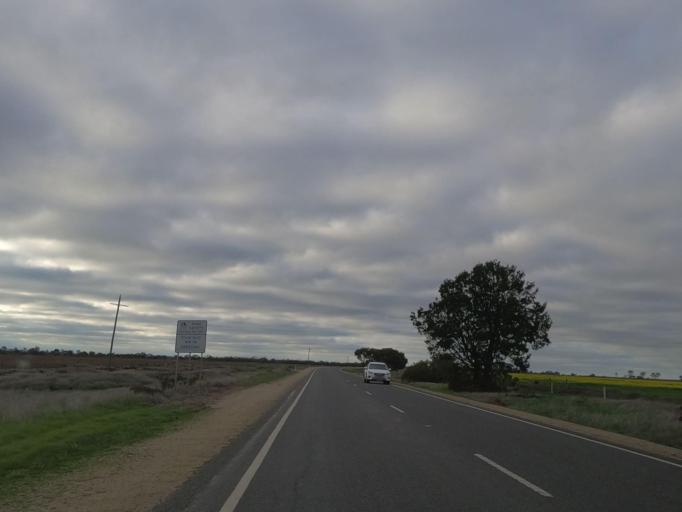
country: AU
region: Victoria
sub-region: Swan Hill
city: Swan Hill
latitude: -35.8301
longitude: 143.9445
